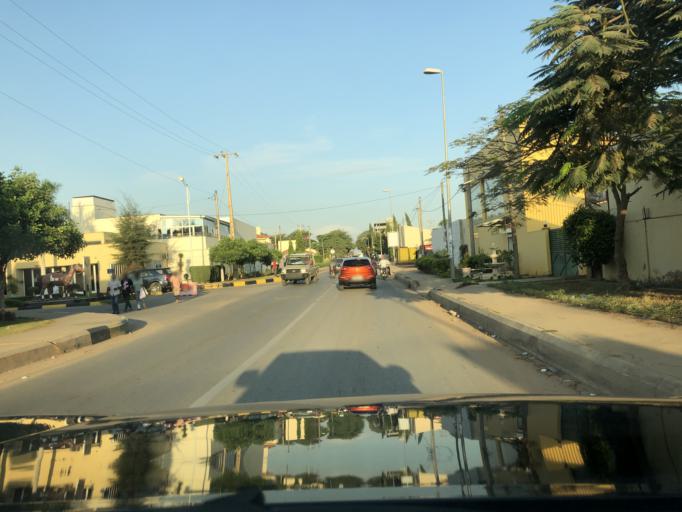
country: AO
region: Luanda
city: Luanda
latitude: -8.9461
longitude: 13.1622
